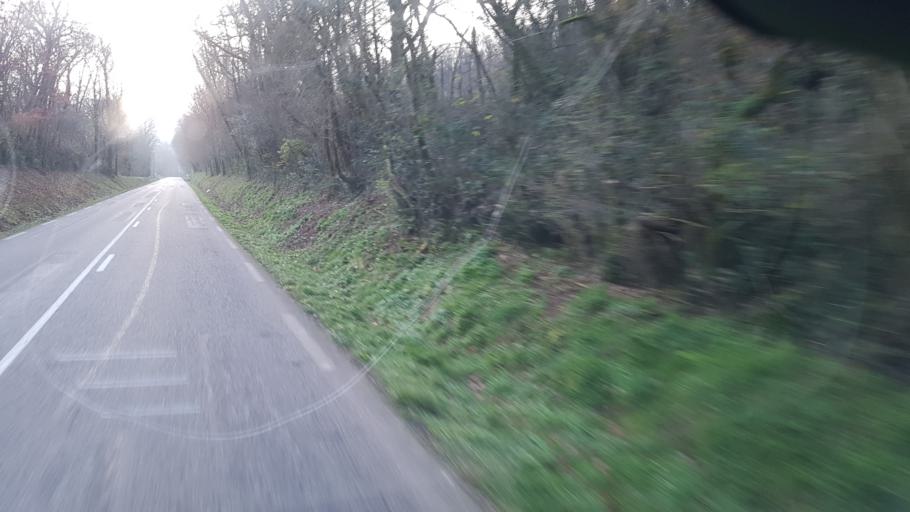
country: FR
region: Midi-Pyrenees
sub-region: Departement du Tarn-et-Garonne
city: Montricoux
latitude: 44.0662
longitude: 1.6582
